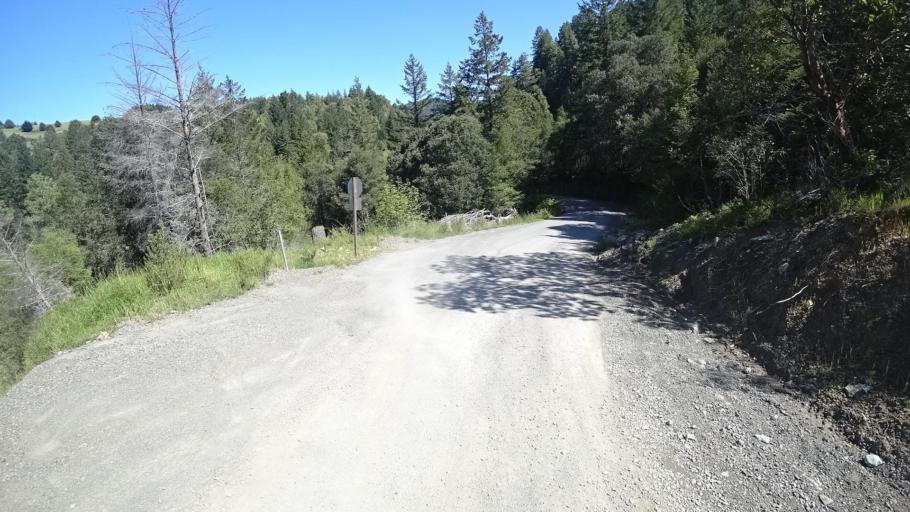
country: US
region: California
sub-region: Humboldt County
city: Rio Dell
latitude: 40.2200
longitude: -124.1117
